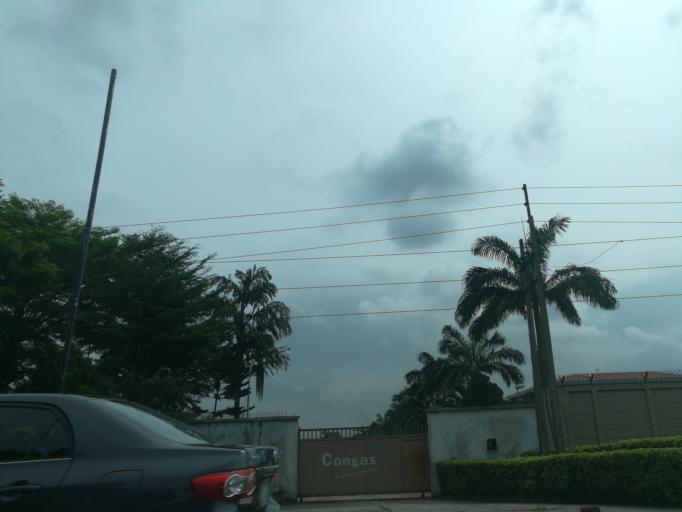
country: NG
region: Lagos
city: Ojota
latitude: 6.6082
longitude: 3.3690
